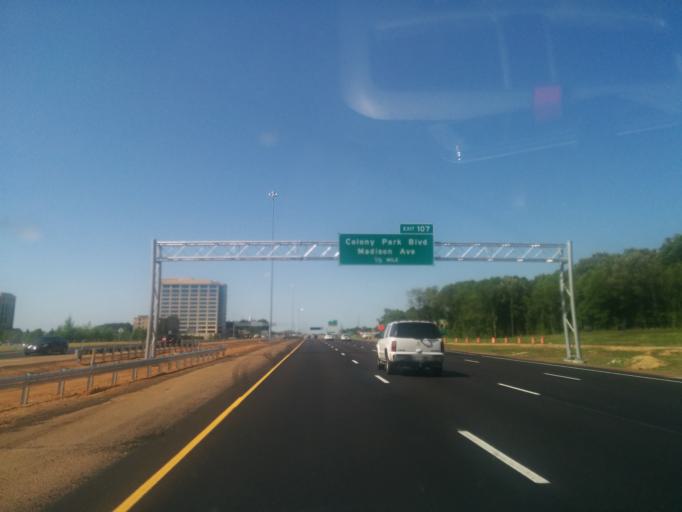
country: US
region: Mississippi
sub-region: Madison County
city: Ridgeland
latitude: 32.4328
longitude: -90.1440
